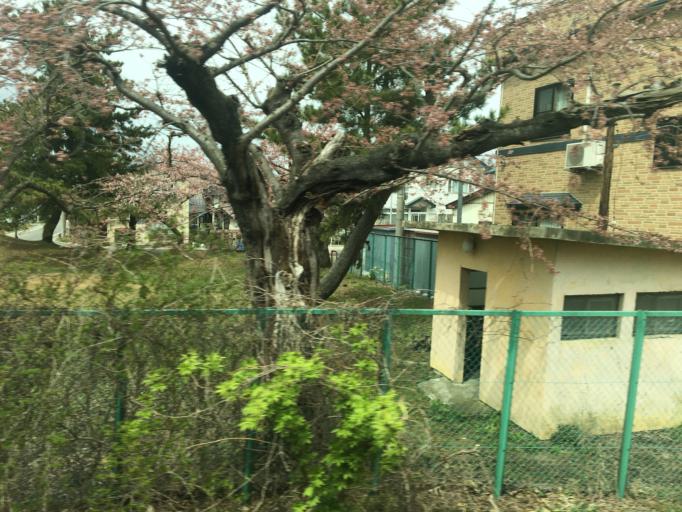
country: JP
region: Aomori
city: Shimokizukuri
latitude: 40.8044
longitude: 140.3942
